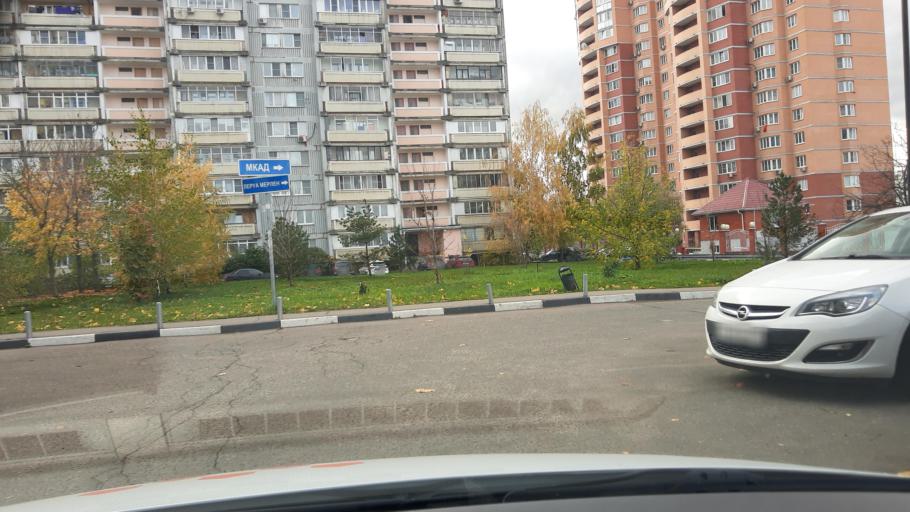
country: RU
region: Moskovskaya
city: Razvilka
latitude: 55.5883
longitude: 37.7286
